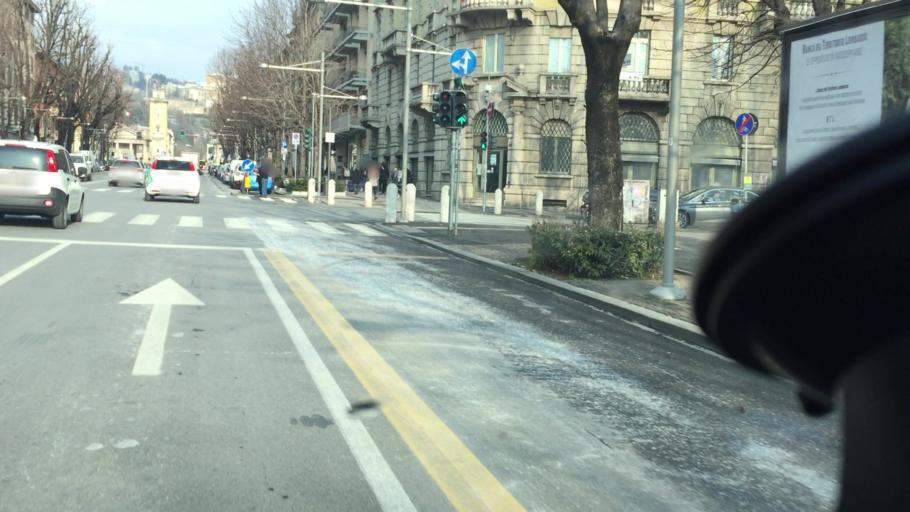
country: IT
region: Lombardy
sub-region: Provincia di Bergamo
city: Bergamo
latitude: 45.6922
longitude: 9.6731
